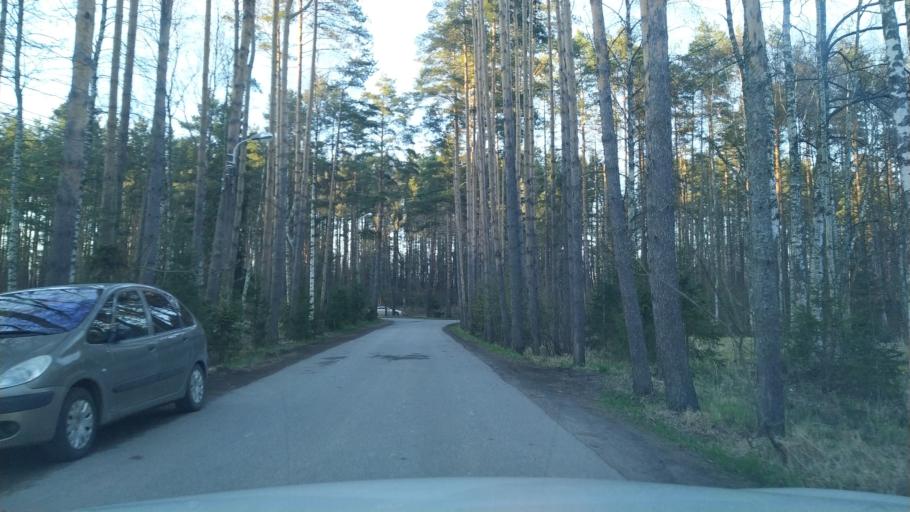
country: RU
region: St.-Petersburg
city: Solnechnoye
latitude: 60.1452
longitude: 29.9465
